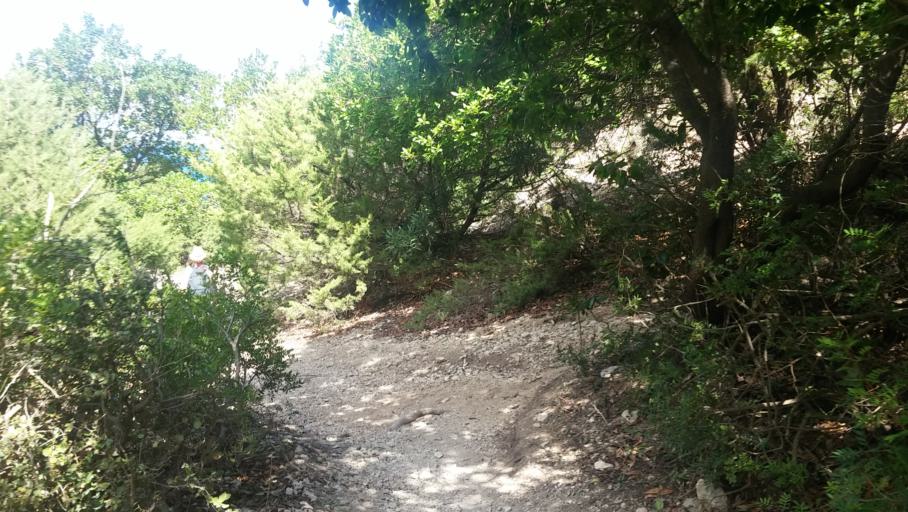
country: IT
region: Sardinia
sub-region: Provincia di Ogliastra
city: Baunei
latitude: 40.1071
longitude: 9.6898
